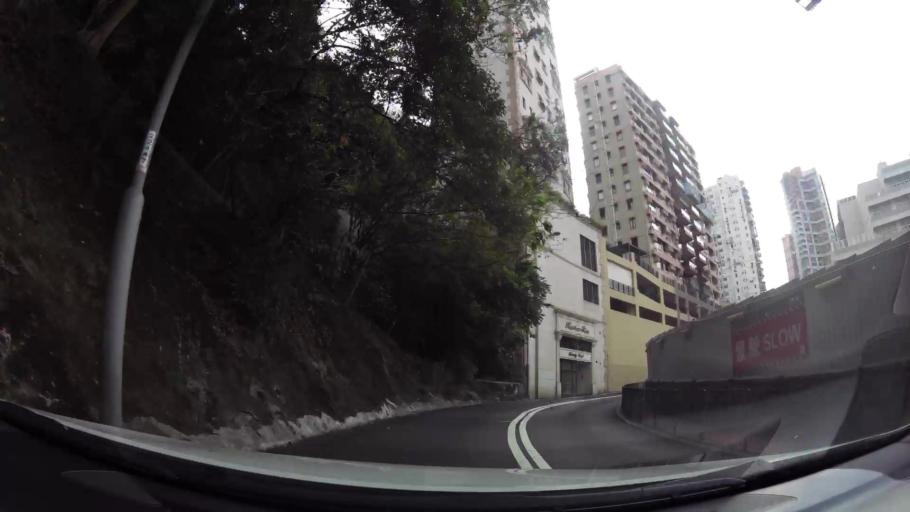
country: HK
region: Wanchai
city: Wan Chai
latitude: 22.2743
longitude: 114.1701
